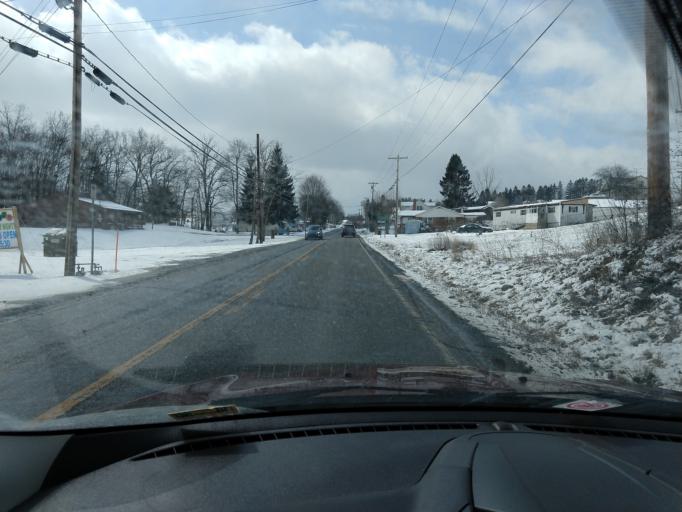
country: US
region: West Virginia
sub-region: Nicholas County
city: Craigsville
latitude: 38.3338
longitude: -80.6413
